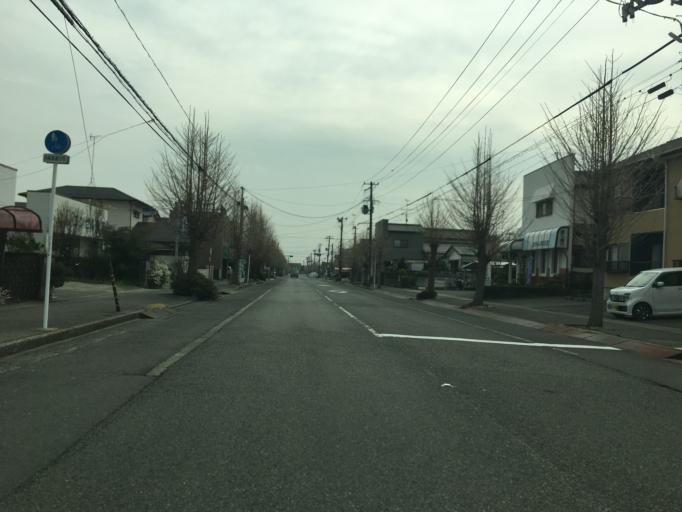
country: JP
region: Fukushima
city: Iwaki
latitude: 36.9836
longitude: 140.8867
